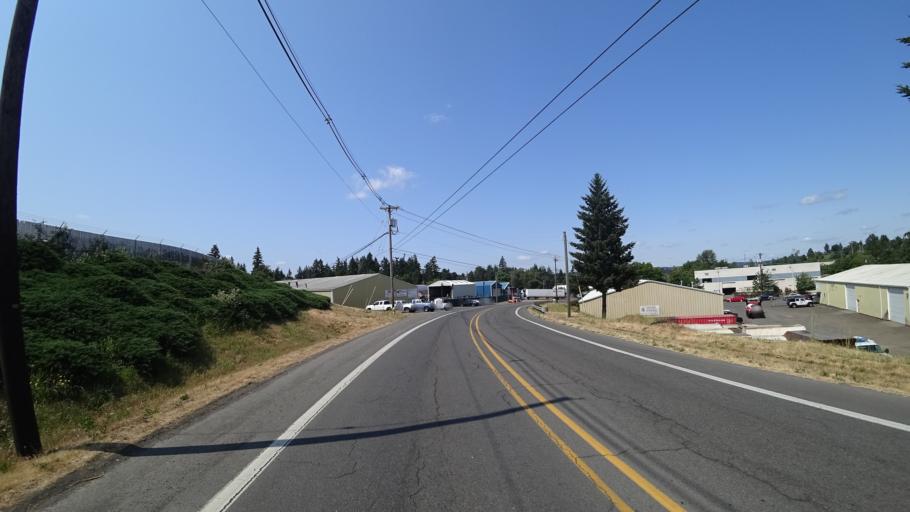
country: US
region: Oregon
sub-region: Multnomah County
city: Lents
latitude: 45.4563
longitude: -122.5867
